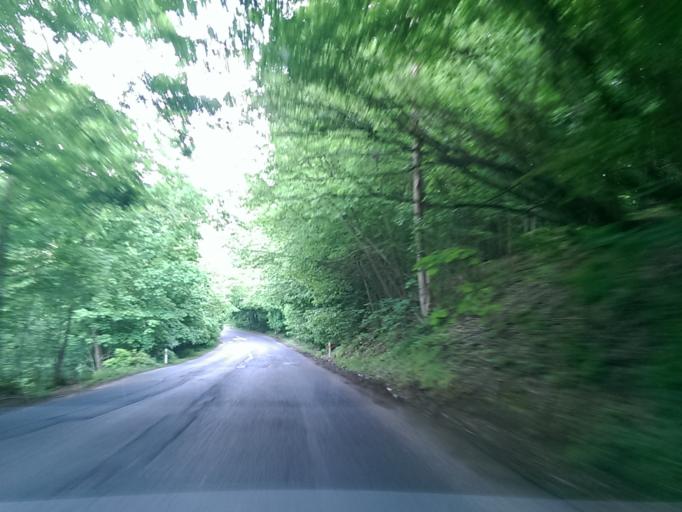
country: CZ
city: Duba
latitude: 50.5499
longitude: 14.5483
